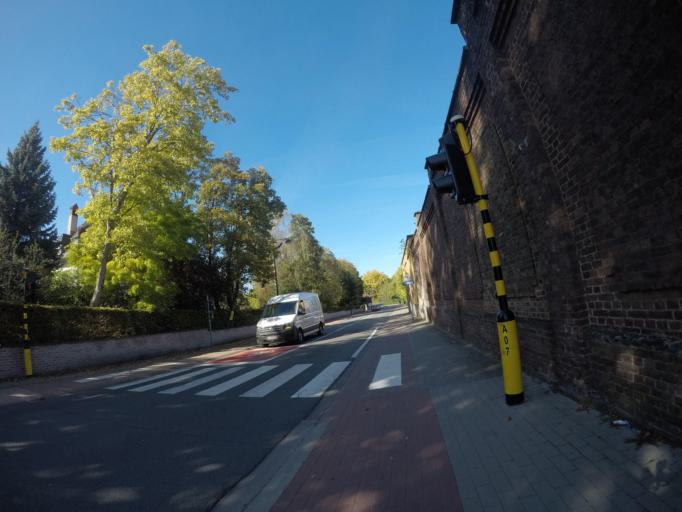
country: BE
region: Flanders
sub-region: Provincie Limburg
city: Alken
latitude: 50.8769
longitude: 5.3070
